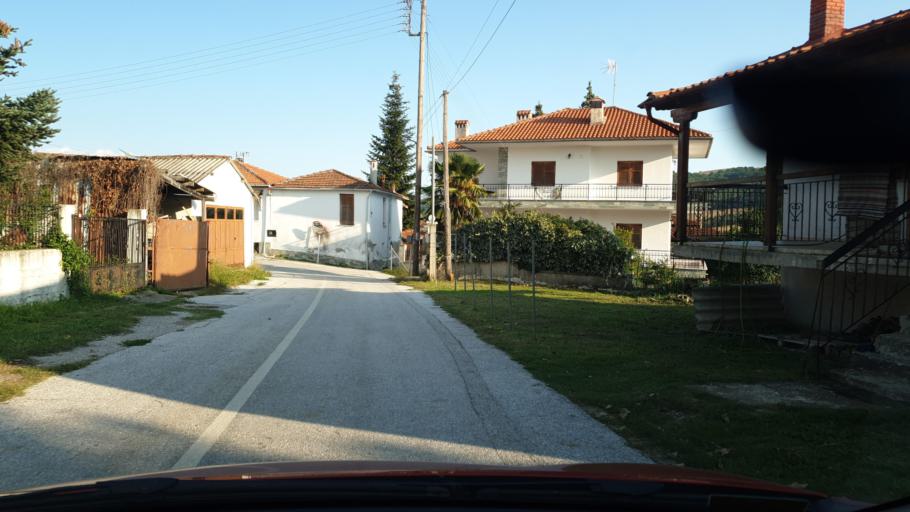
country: GR
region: Central Macedonia
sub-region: Nomos Chalkidikis
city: Galatista
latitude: 40.5169
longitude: 23.2827
